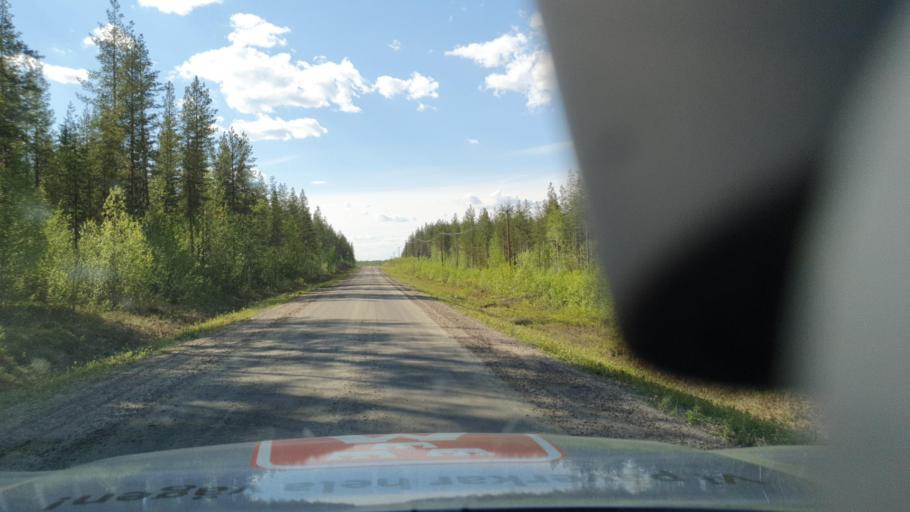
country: SE
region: Norrbotten
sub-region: Lulea Kommun
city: Ranea
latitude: 66.5623
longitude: 22.1549
